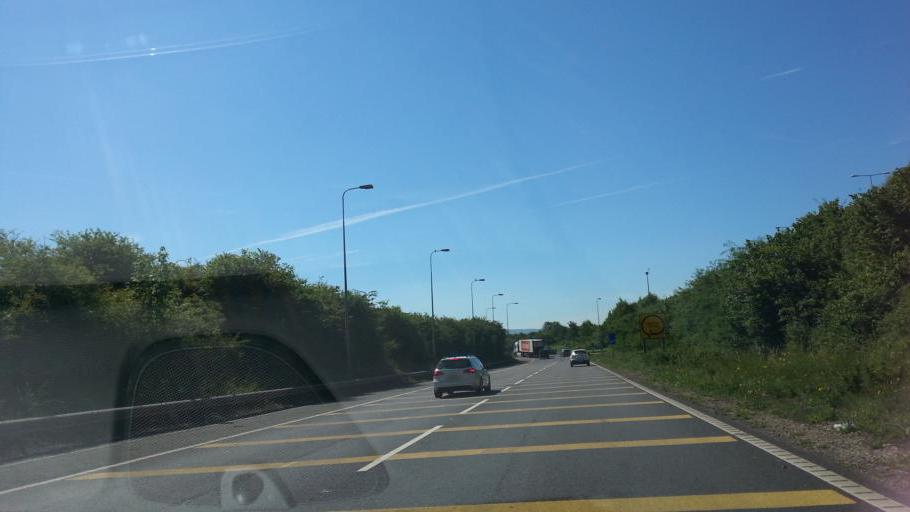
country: GB
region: England
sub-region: Worcestershire
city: Bredon
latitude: 52.0502
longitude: -2.1365
